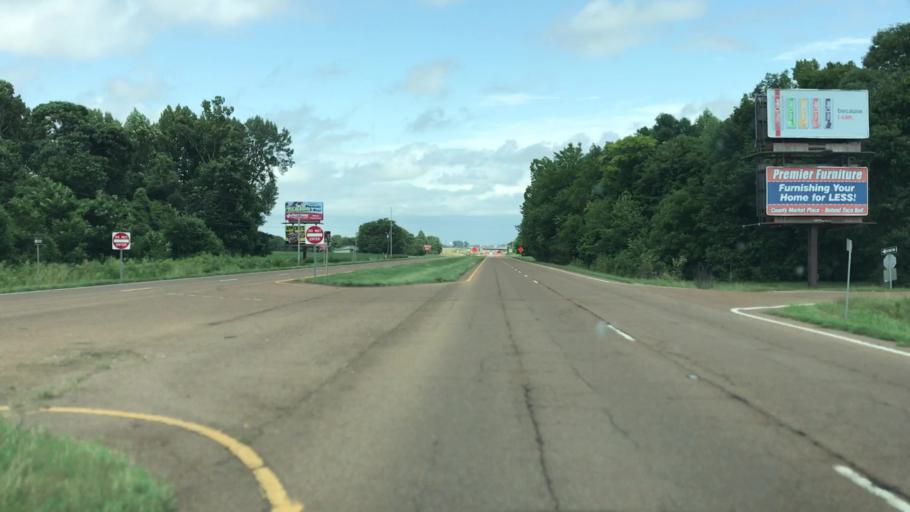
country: US
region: Tennessee
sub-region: Obion County
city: Englewood
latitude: 36.3855
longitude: -89.1068
